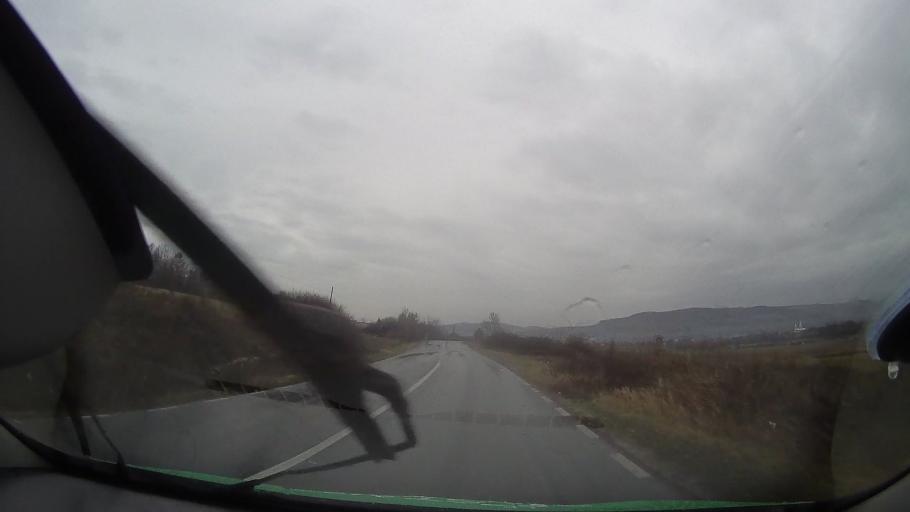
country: RO
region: Bihor
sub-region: Comuna Rabagani
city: Rabagani
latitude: 46.7394
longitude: 22.2297
